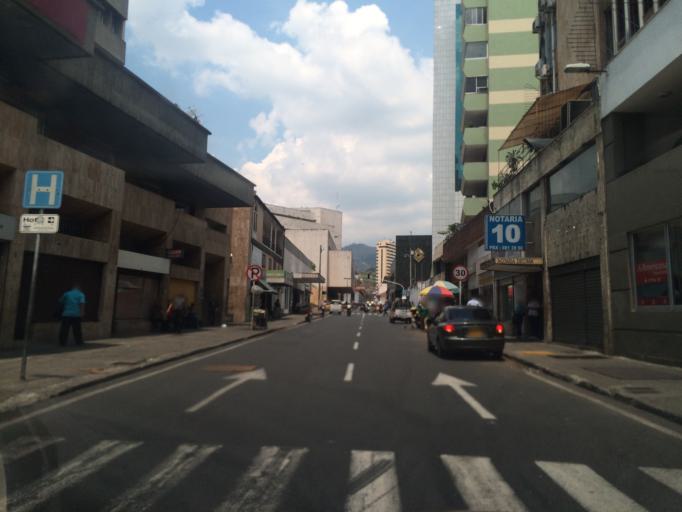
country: CO
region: Valle del Cauca
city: Cali
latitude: 3.4513
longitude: -76.5345
